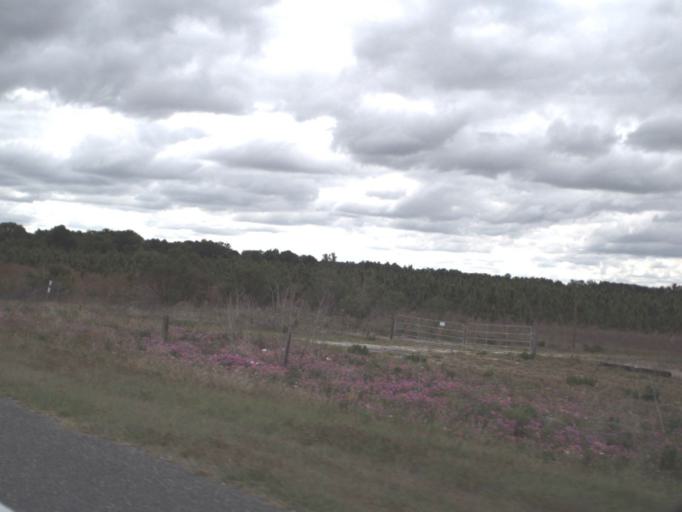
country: US
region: Florida
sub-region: Marion County
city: Ocala
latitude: 29.2594
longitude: -82.0765
